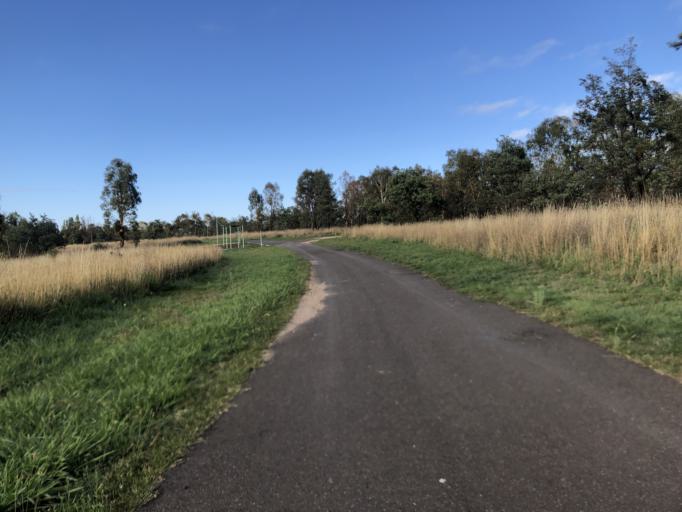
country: AU
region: New South Wales
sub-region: Orange Municipality
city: Orange
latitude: -33.3274
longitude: 149.0854
